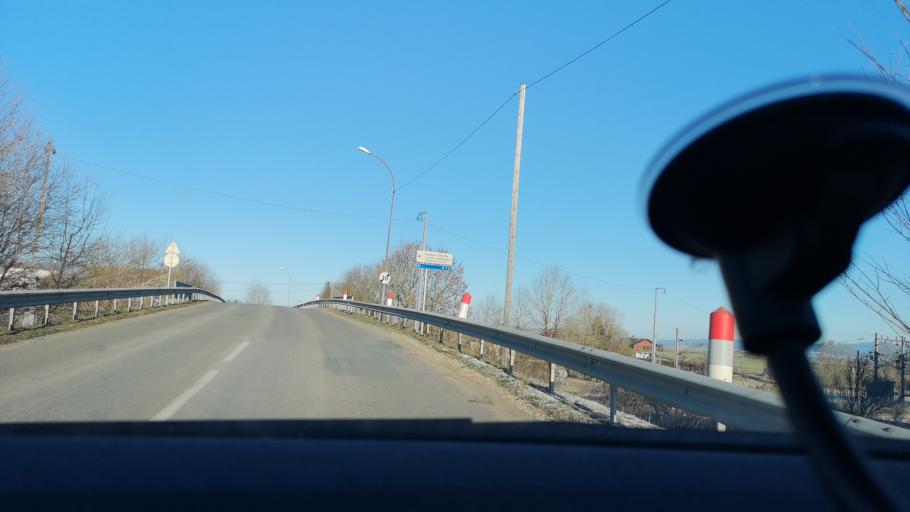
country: FR
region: Franche-Comte
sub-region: Departement du Doubs
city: Frasne
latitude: 46.8588
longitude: 6.1649
